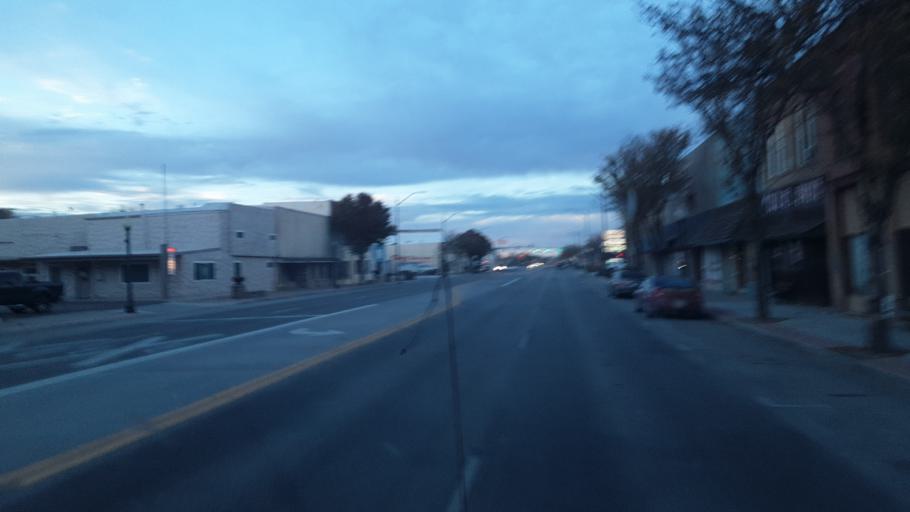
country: US
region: Colorado
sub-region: Prowers County
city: Lamar
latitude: 38.0903
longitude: -102.6193
